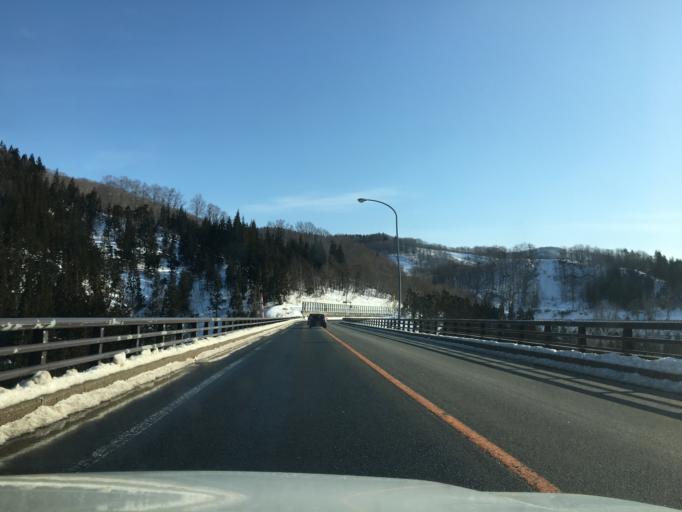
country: JP
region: Yamagata
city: Tsuruoka
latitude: 38.5785
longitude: 139.9432
